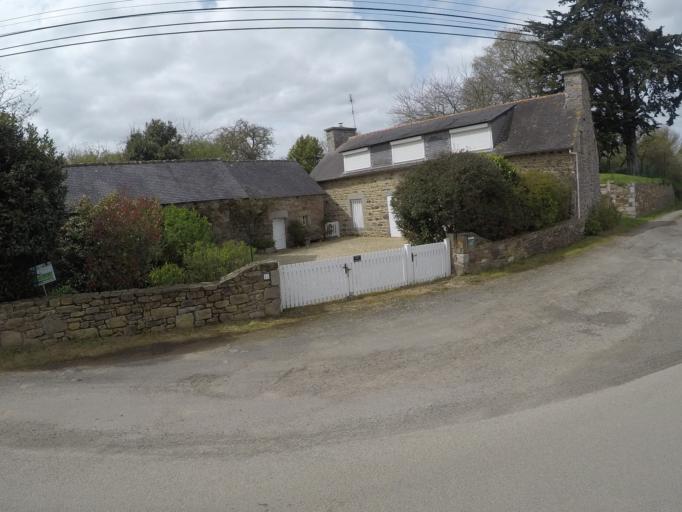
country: FR
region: Brittany
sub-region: Departement des Cotes-d'Armor
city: Plouezec
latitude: 48.7206
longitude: -2.9529
